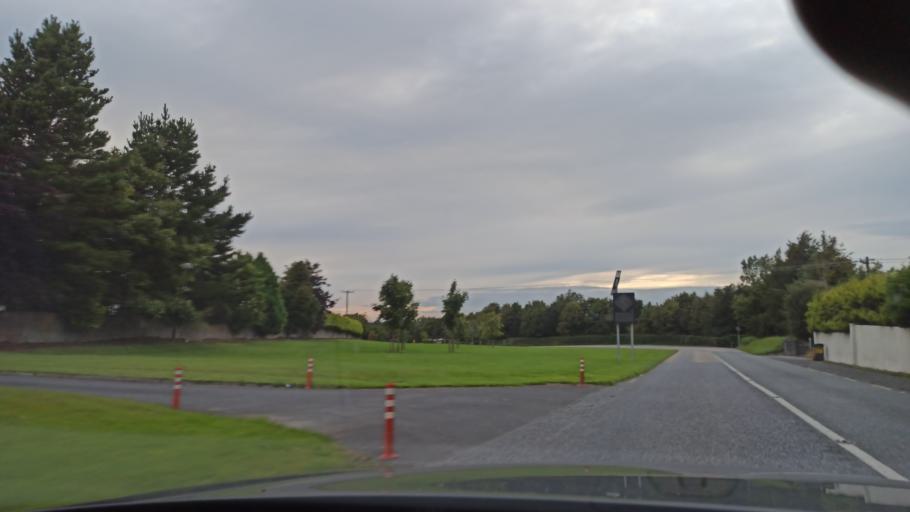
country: IE
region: Munster
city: Cashel
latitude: 52.4745
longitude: -7.8401
